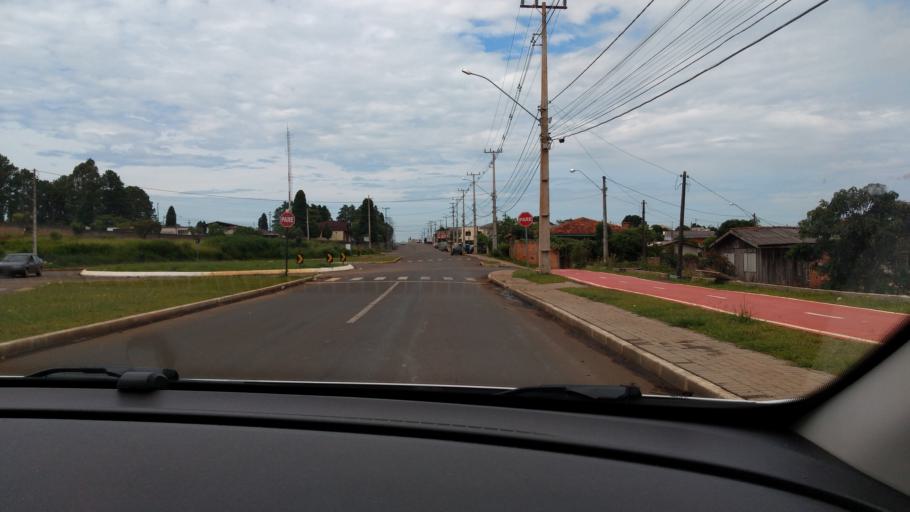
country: BR
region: Parana
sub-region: Guarapuava
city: Guarapuava
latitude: -25.3712
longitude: -51.4413
